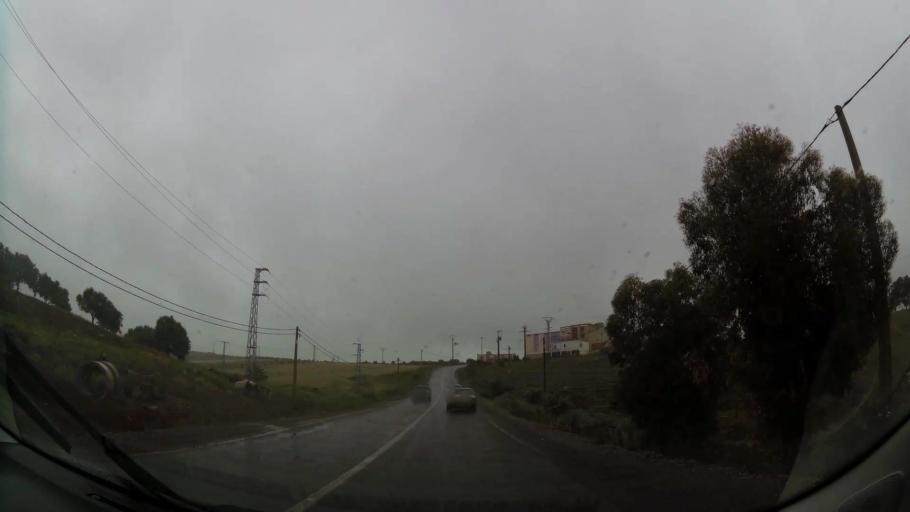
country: MA
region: Oriental
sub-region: Nador
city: Boudinar
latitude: 35.1313
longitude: -3.6279
